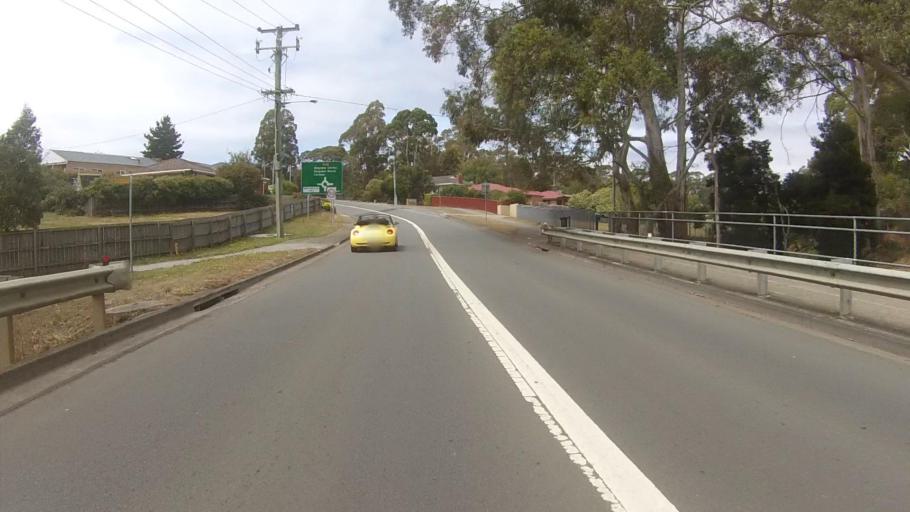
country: AU
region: Tasmania
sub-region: Kingborough
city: Kingston
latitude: -42.9737
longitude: 147.2995
